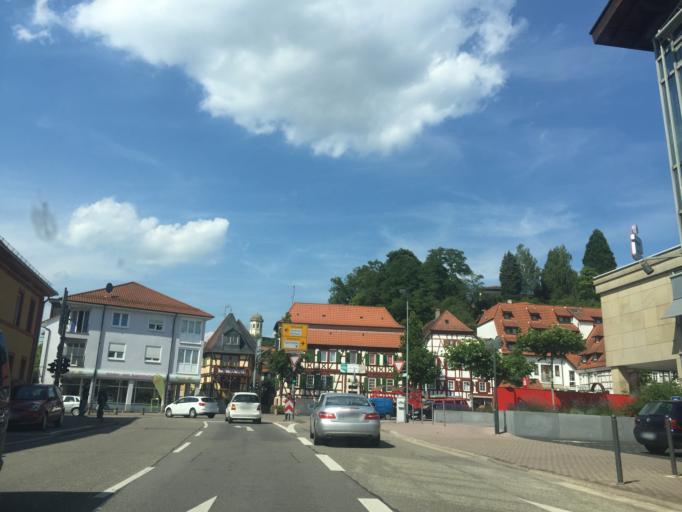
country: DE
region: Baden-Wuerttemberg
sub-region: Karlsruhe Region
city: Sinsheim
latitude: 49.2523
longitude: 8.8797
